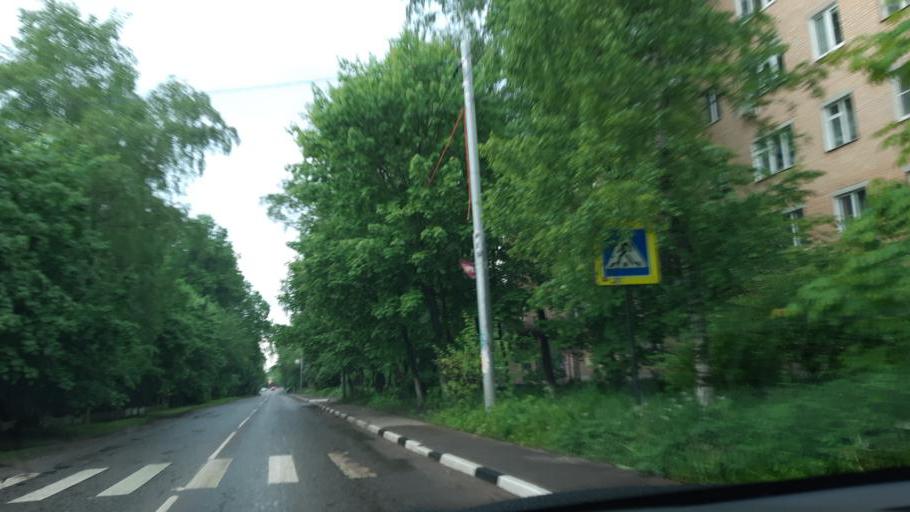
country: RU
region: Moskovskaya
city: Bol'shiye Vyazemy
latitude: 55.6266
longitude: 36.9935
